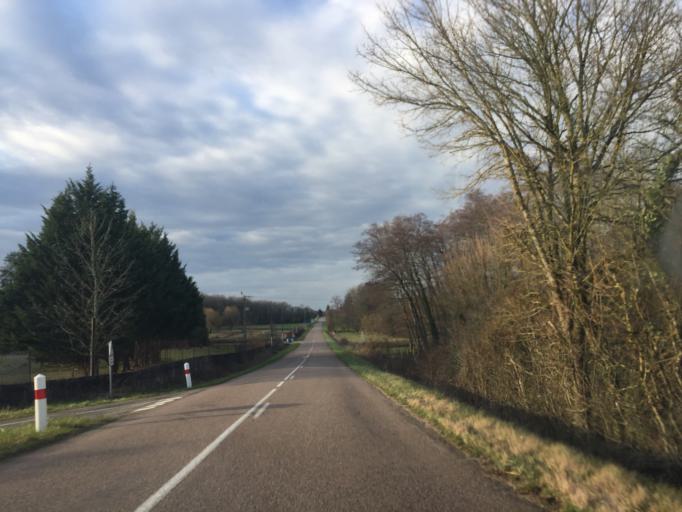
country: FR
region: Franche-Comte
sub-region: Departement du Jura
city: Arbois
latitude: 46.9271
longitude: 5.6882
